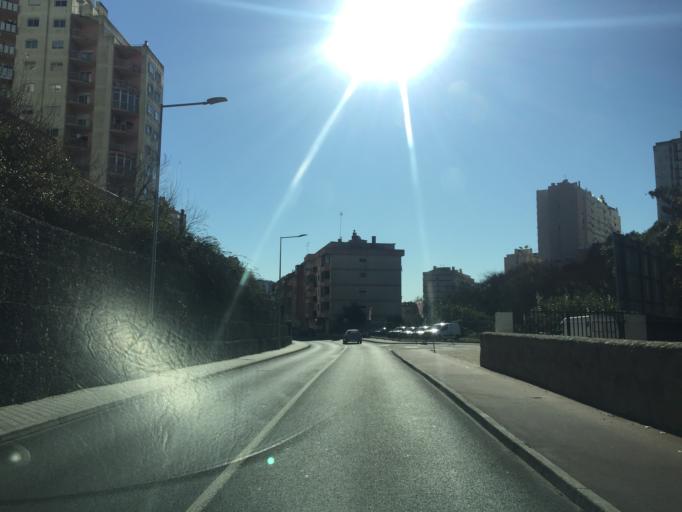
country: PT
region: Lisbon
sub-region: Sintra
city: Belas
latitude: 38.7686
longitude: -9.2593
